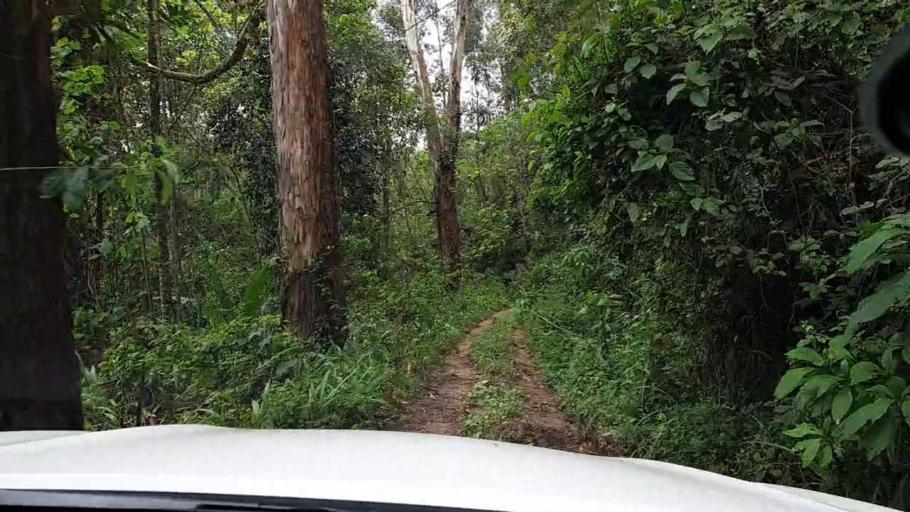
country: RW
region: Western Province
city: Kibuye
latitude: -2.2852
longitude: 29.3045
